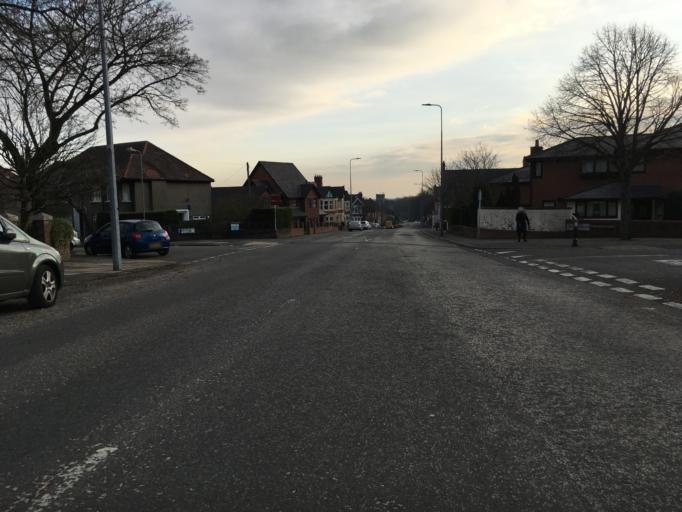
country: GB
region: Wales
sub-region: Cardiff
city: Cardiff
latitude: 51.4980
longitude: -3.1571
